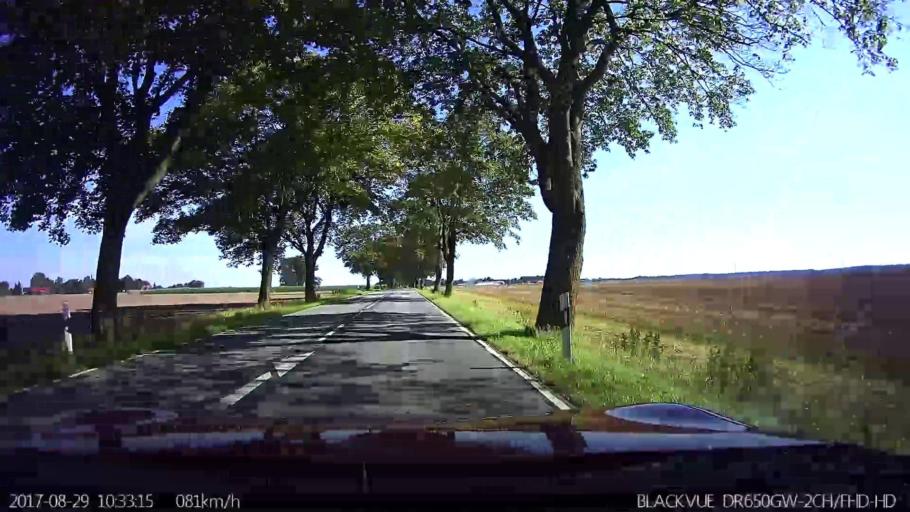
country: DE
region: Mecklenburg-Vorpommern
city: Tribsees
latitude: 54.1160
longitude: 12.7729
